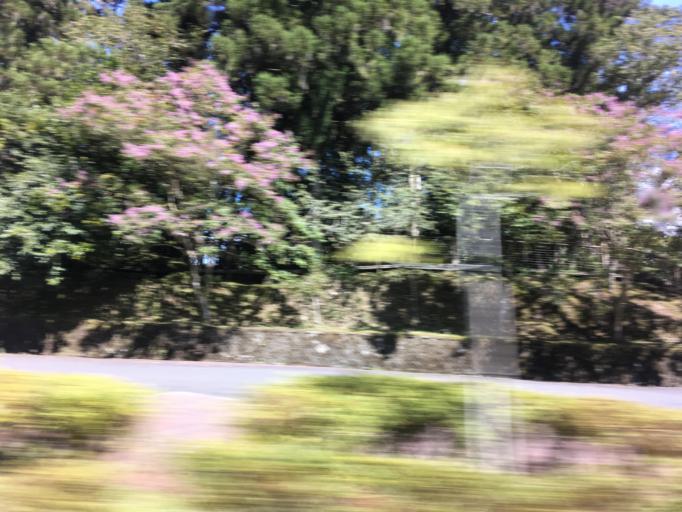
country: TW
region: Taiwan
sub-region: Yilan
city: Yilan
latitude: 24.5414
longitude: 121.5129
